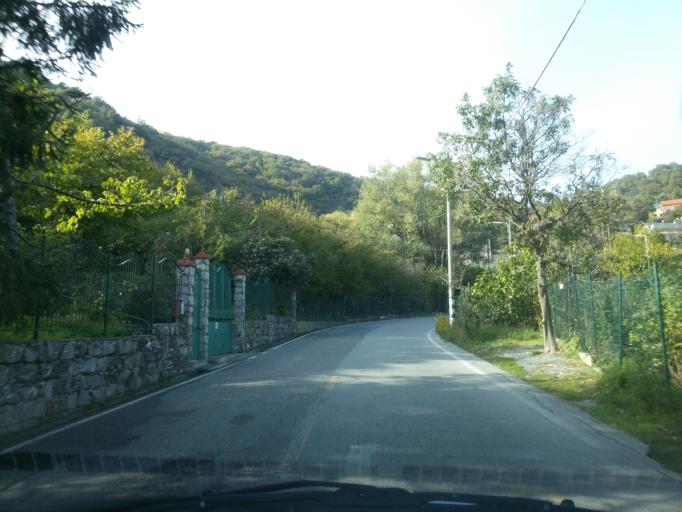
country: IT
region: Liguria
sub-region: Provincia di Genova
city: Piccarello
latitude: 44.4642
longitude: 8.9644
